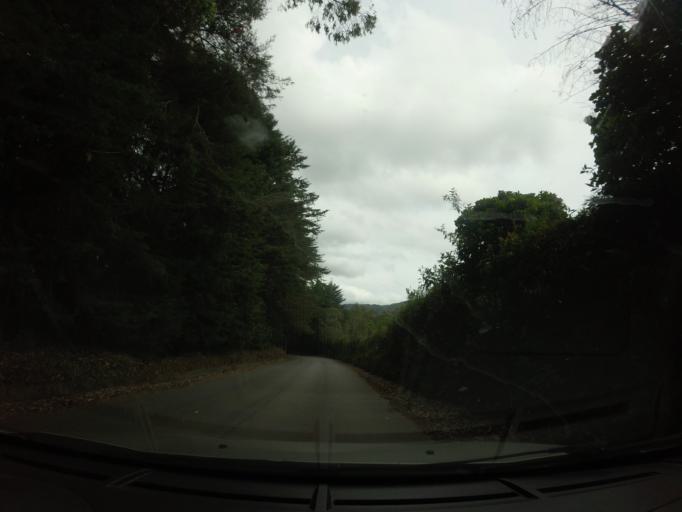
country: BR
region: Sao Paulo
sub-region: Campos Do Jordao
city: Campos do Jordao
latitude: -22.6709
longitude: -45.5944
